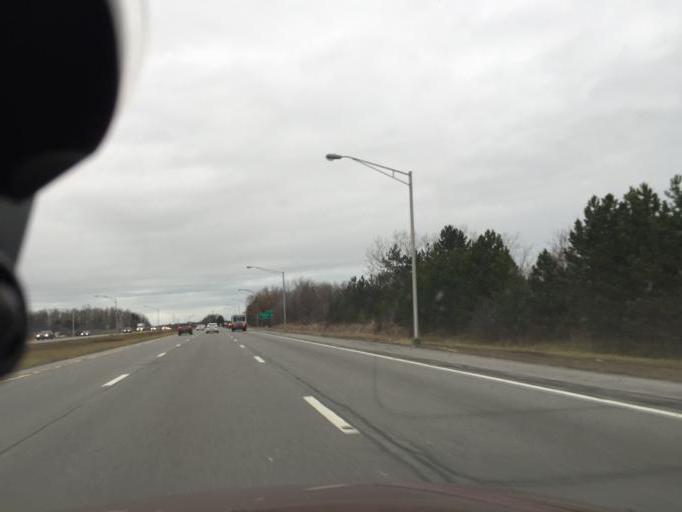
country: US
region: New York
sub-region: Monroe County
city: North Gates
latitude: 43.1857
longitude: -77.6834
